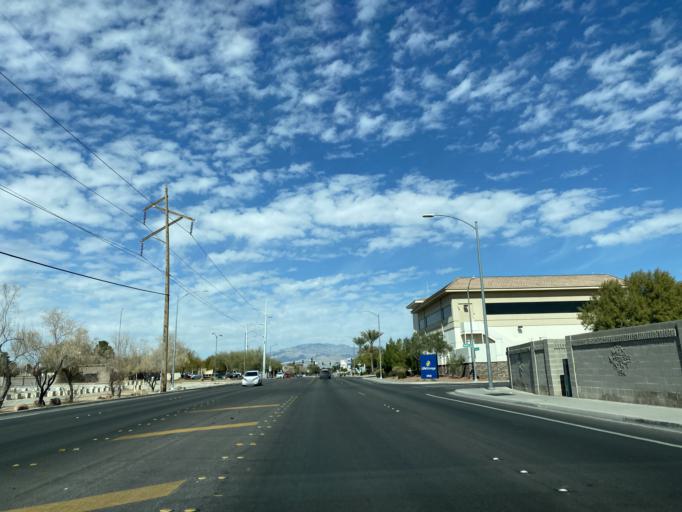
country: US
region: Nevada
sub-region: Clark County
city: Spring Valley
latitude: 36.2309
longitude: -115.2514
